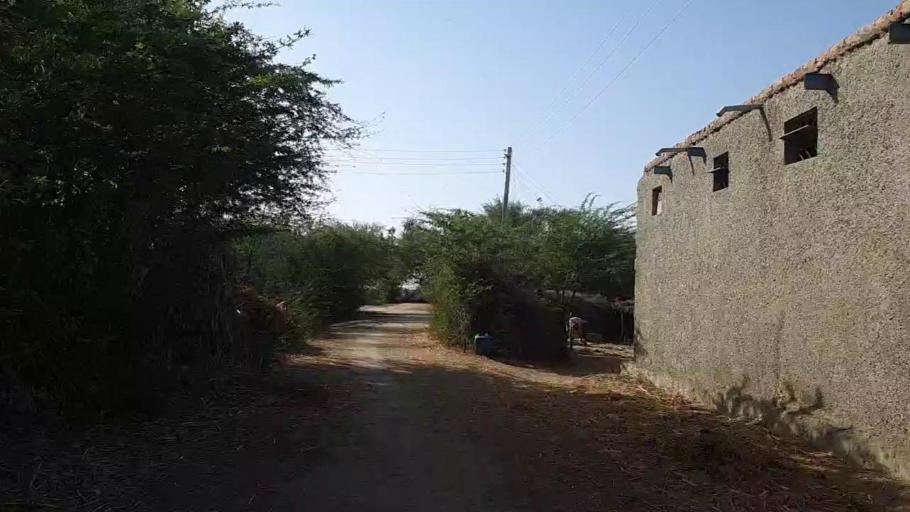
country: PK
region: Sindh
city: Kotri
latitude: 25.1400
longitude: 68.2899
